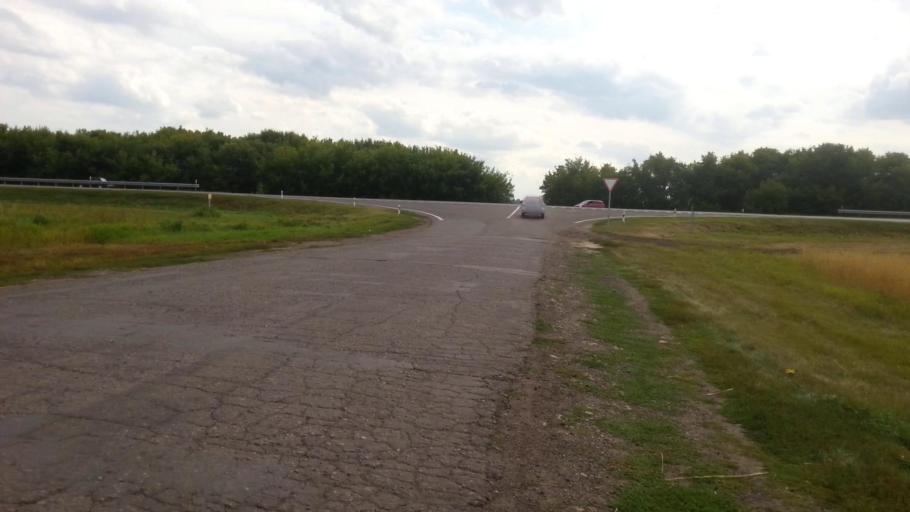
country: RU
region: Altai Krai
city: Nauchnyy Gorodok
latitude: 53.3574
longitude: 83.5081
